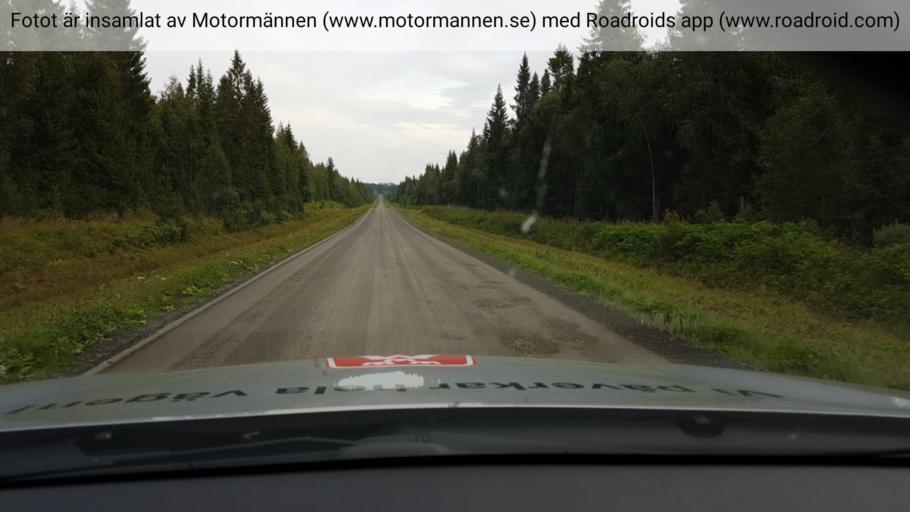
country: SE
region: Jaemtland
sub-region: OEstersunds Kommun
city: Lit
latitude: 63.6572
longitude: 14.9224
